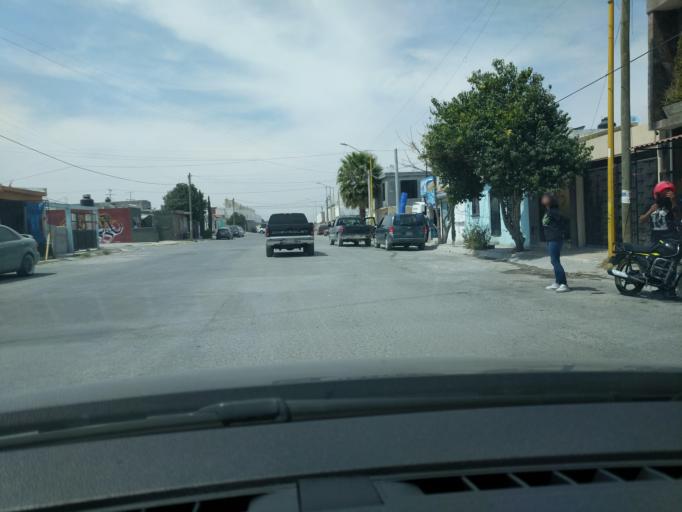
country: MX
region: Coahuila
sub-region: Arteaga
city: Arteaga
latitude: 25.4276
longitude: -100.9104
